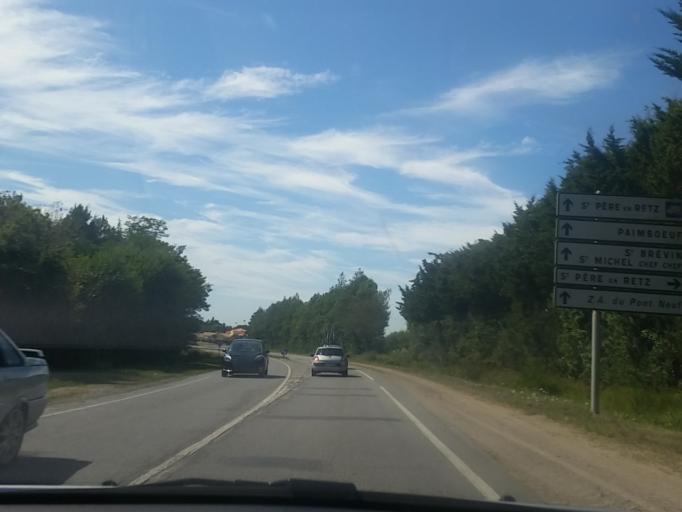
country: FR
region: Pays de la Loire
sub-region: Departement de la Loire-Atlantique
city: Saint-Pere-en-Retz
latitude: 47.1998
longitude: -2.0348
